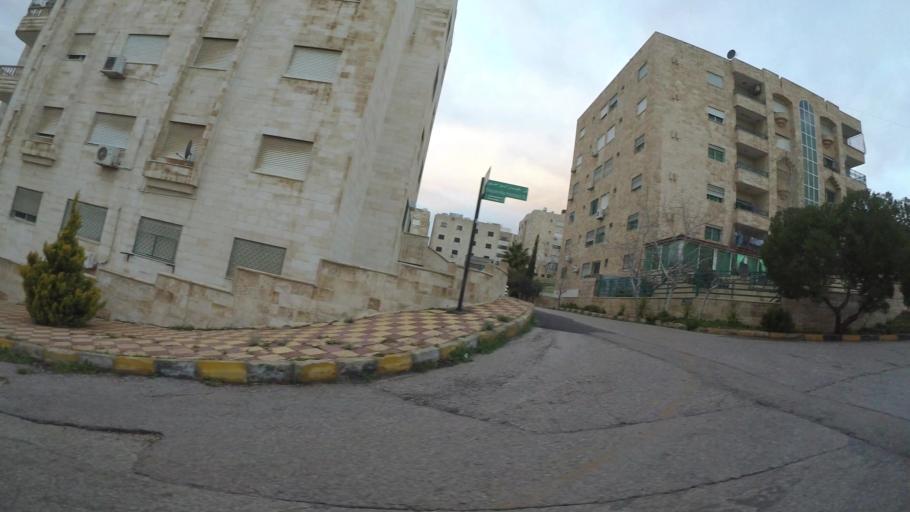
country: JO
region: Amman
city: Amman
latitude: 31.9859
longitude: 35.9124
